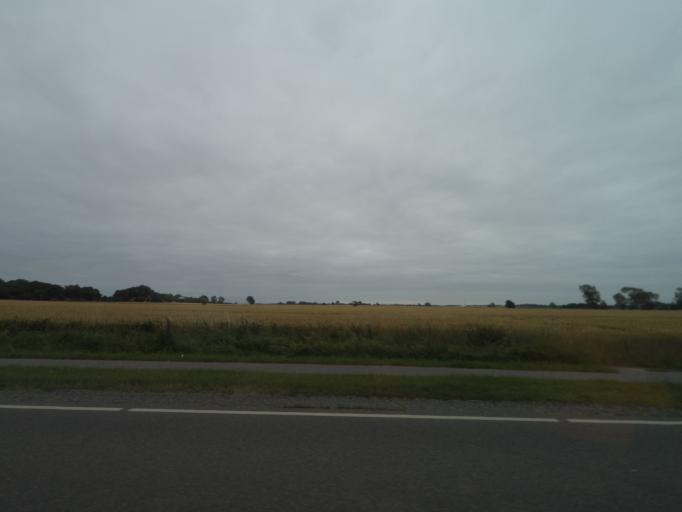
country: DK
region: South Denmark
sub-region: Nordfyns Kommune
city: Otterup
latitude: 55.5368
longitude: 10.4270
